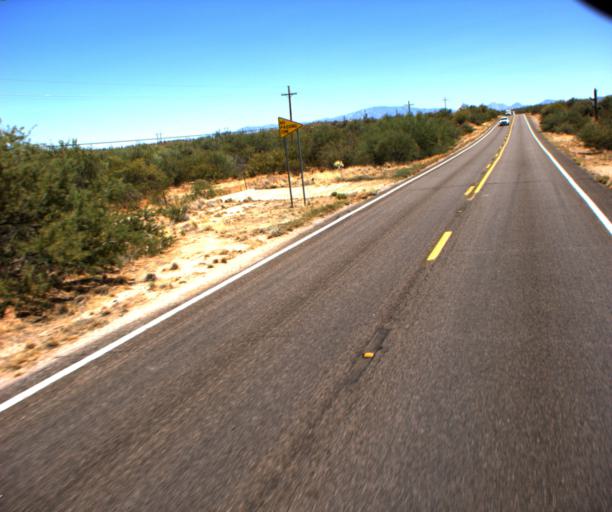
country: US
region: Arizona
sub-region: Pima County
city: Catalina
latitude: 32.7109
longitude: -111.1004
